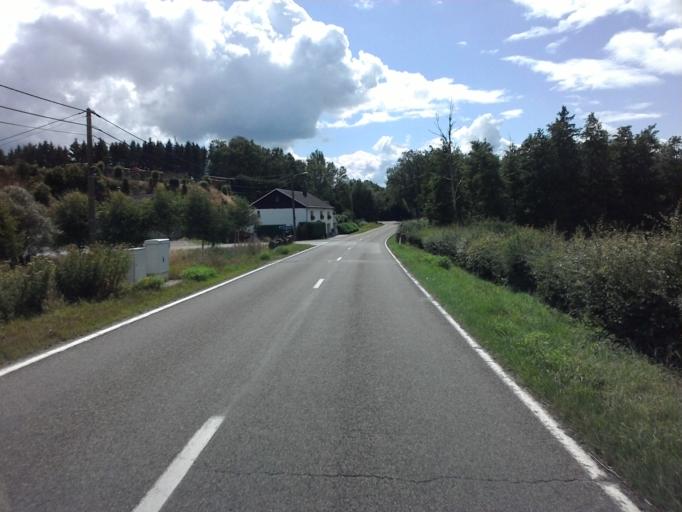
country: BE
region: Wallonia
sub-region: Province du Luxembourg
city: Habay-la-Vieille
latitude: 49.7821
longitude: 5.6074
